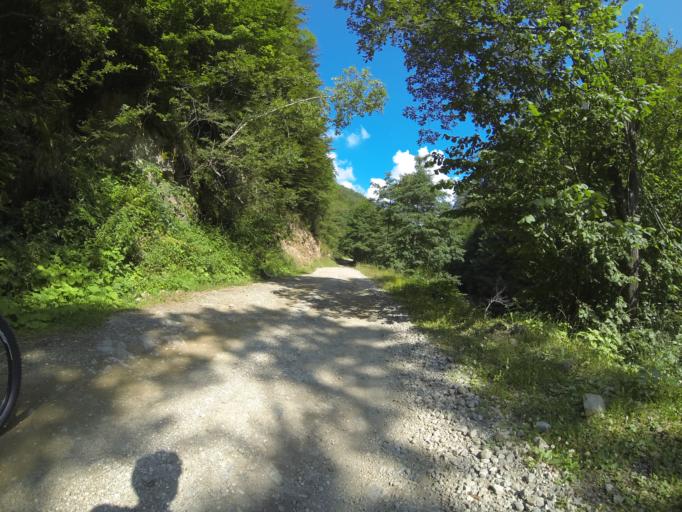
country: RO
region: Valcea
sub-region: Comuna Costesti
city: Bistrita
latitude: 45.2437
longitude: 23.9970
